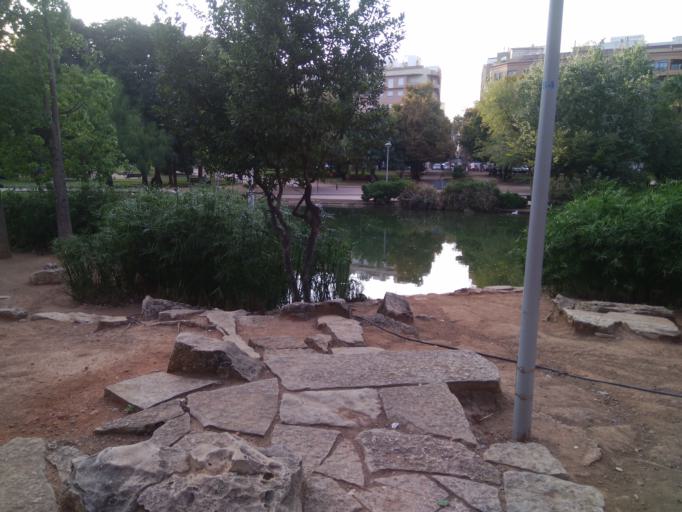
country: ES
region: Valencia
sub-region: Provincia de Castello
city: Castello de la Plana
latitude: 39.9781
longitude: -0.0375
